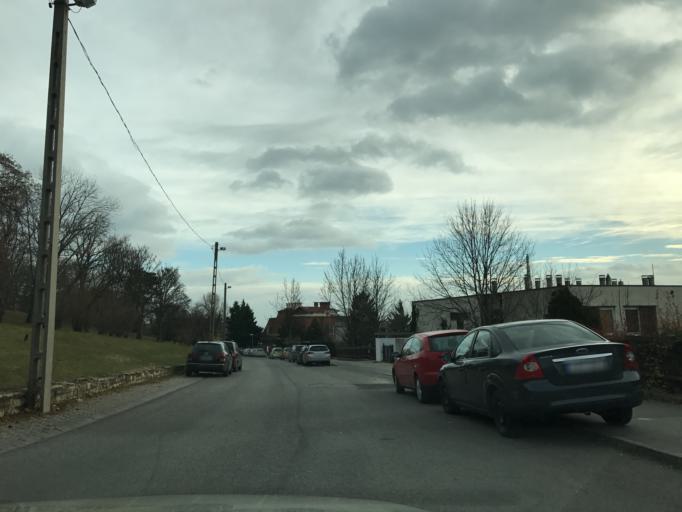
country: HU
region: Budapest
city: Budapest XI. keruelet
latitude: 47.4849
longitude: 19.0410
